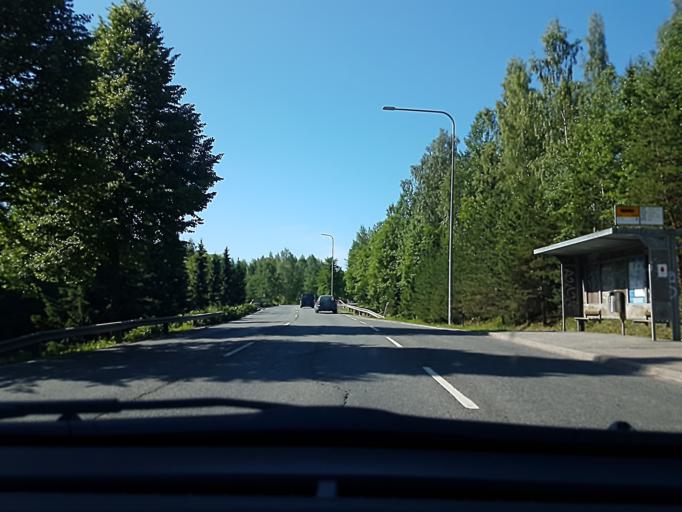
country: FI
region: Uusimaa
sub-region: Helsinki
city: Vantaa
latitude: 60.3402
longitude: 25.0700
